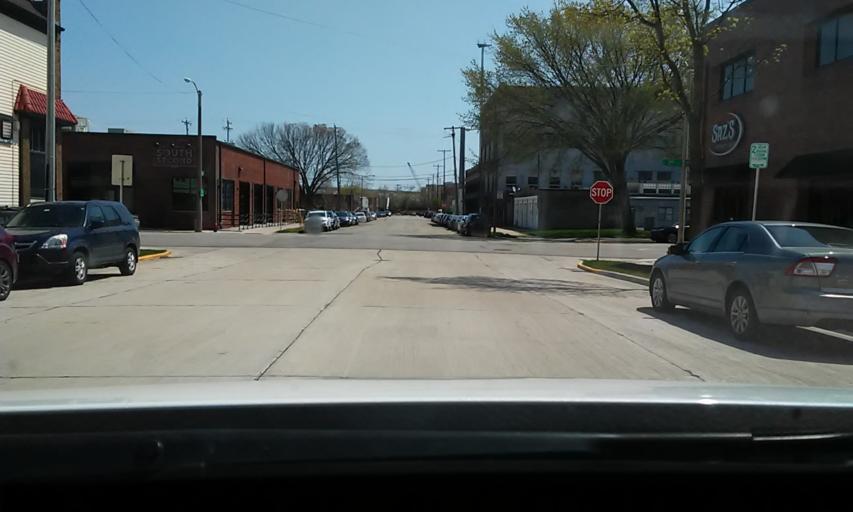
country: US
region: Wisconsin
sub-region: Milwaukee County
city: Milwaukee
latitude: 43.0222
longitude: -87.9131
